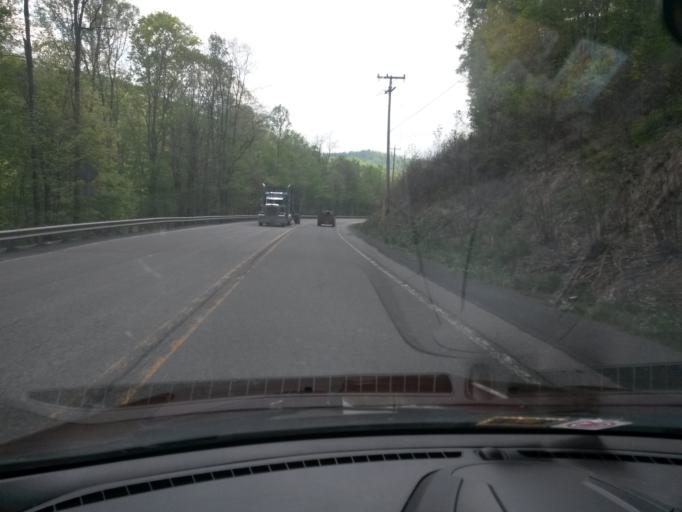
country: US
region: West Virginia
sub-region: Greenbrier County
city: Rainelle
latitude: 38.0131
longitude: -80.7280
